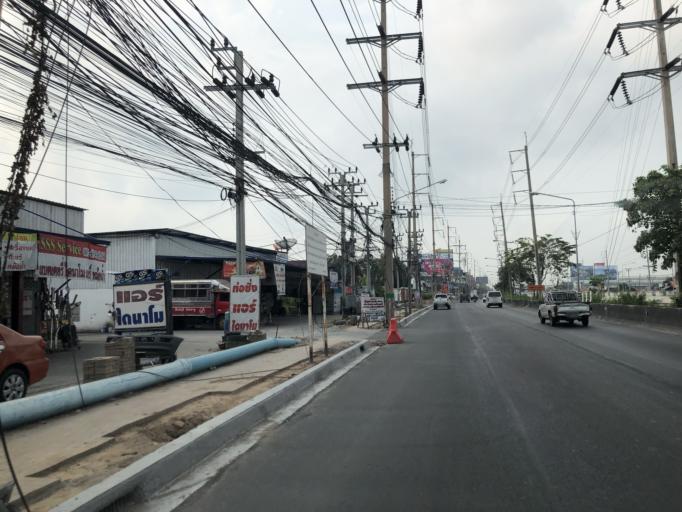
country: TH
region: Bangkok
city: Bang Na
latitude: 13.5884
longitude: 100.6983
